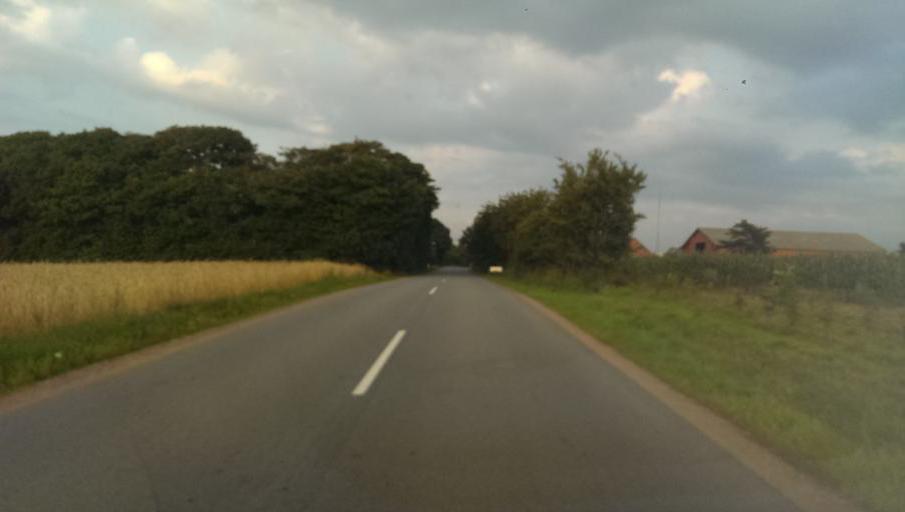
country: DK
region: South Denmark
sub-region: Esbjerg Kommune
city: Tjaereborg
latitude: 55.5558
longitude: 8.6189
